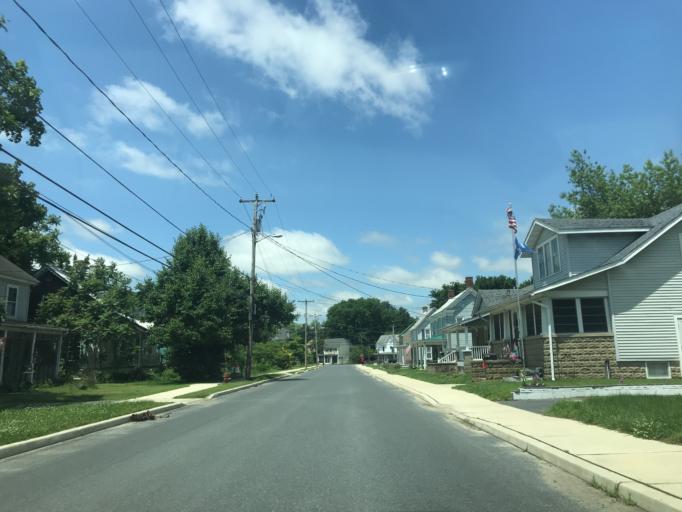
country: US
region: Maryland
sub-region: Caroline County
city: Federalsburg
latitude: 38.6943
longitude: -75.7663
